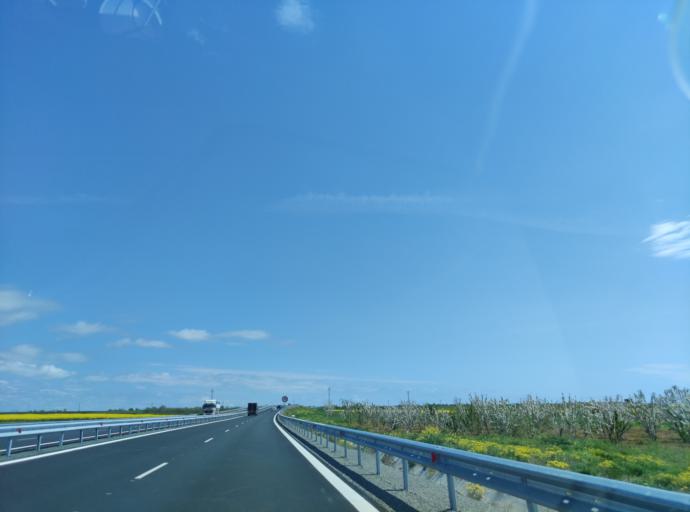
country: BG
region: Burgas
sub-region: Obshtina Pomorie
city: Pomorie
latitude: 42.5760
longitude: 27.5770
